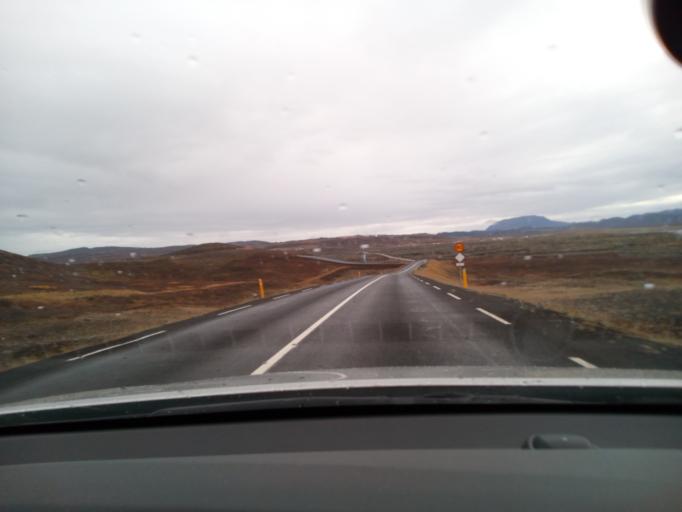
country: IS
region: Northeast
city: Laugar
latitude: 65.6596
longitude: -16.9698
